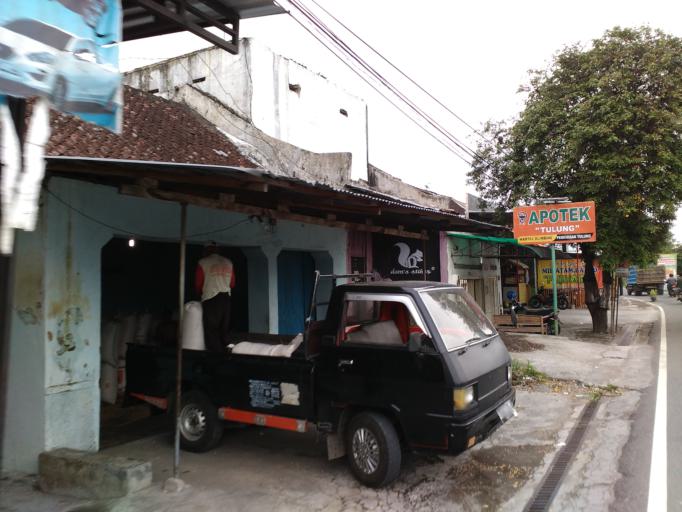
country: ID
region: Central Java
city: Karanganom
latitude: -7.5900
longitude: 110.6217
